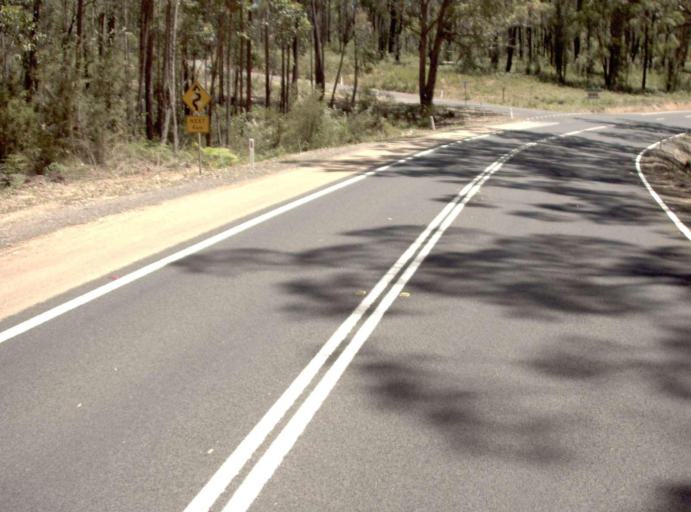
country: AU
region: Victoria
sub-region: East Gippsland
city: Lakes Entrance
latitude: -37.6953
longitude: 148.7435
